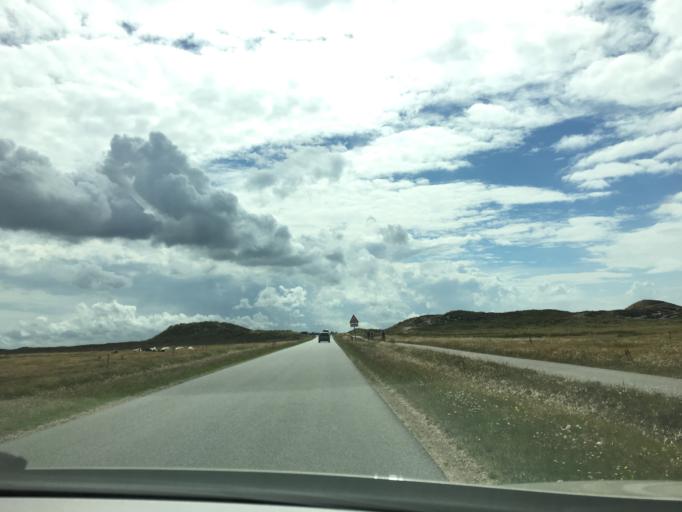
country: DK
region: South Denmark
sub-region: Varde Kommune
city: Oksbol
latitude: 55.7207
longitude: 8.2092
